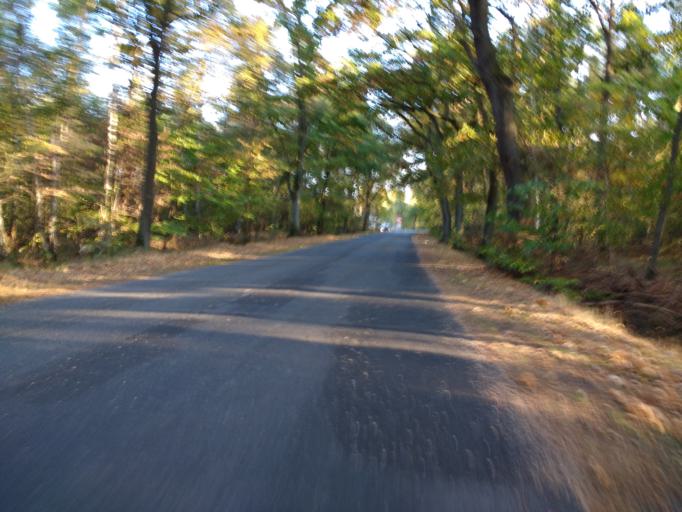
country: DE
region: Lower Saxony
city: Gifhorn
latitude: 52.4638
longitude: 10.5715
